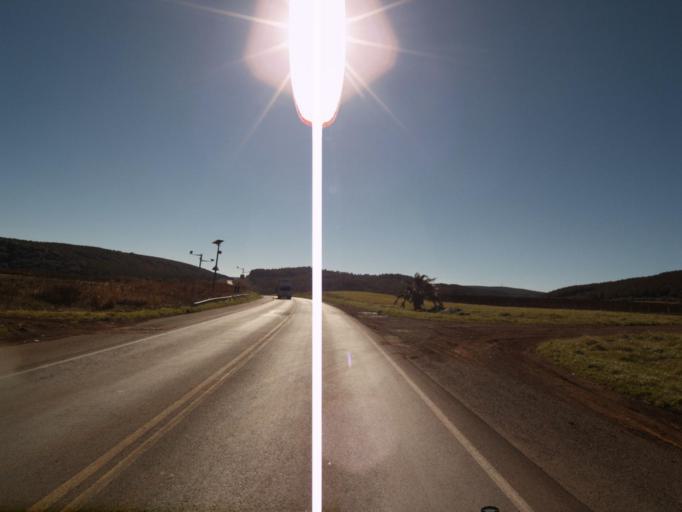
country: BR
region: Parana
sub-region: Palmas
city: Palmas
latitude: -26.6768
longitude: -51.5526
